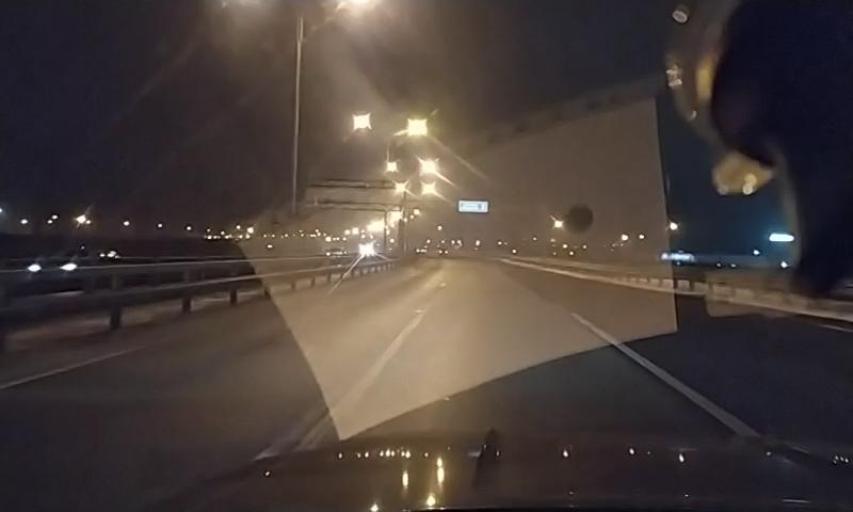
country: RU
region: Leningrad
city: Bugry
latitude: 60.0957
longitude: 30.3780
